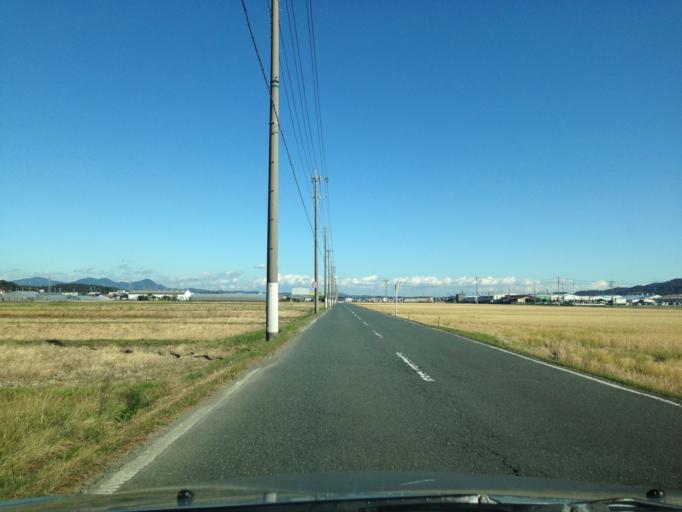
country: JP
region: Shizuoka
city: Fukuroi
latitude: 34.7522
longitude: 137.9317
